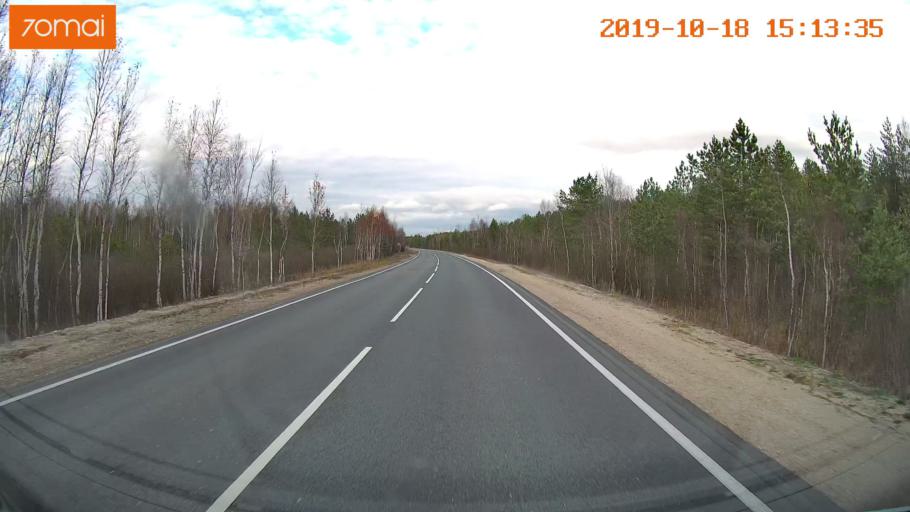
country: RU
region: Vladimir
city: Gus'-Khrustal'nyy
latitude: 55.5892
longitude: 40.7178
